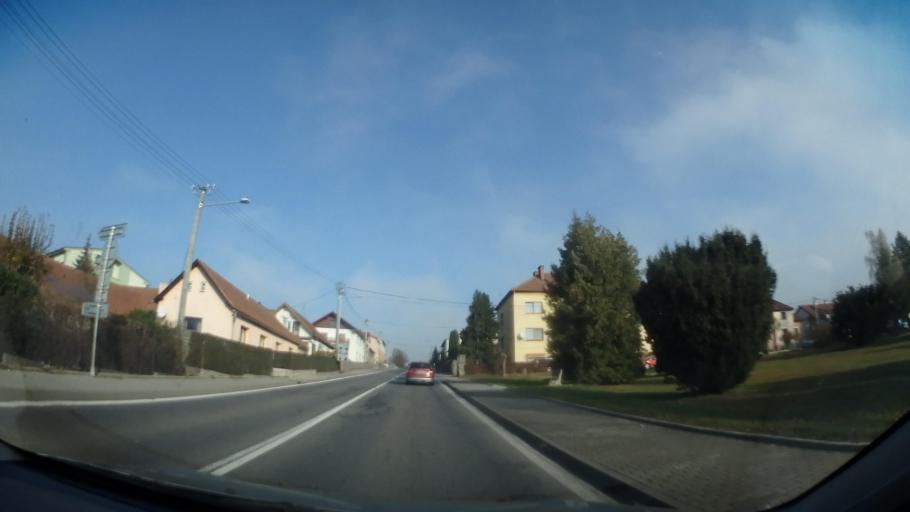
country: CZ
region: Vysocina
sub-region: Okres Zd'ar nad Sazavou
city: Nove Veseli
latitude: 49.4897
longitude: 15.9876
